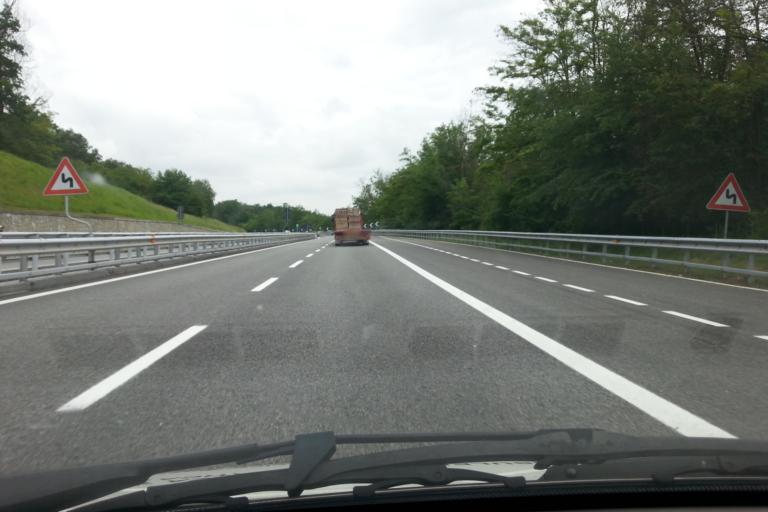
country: IT
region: Piedmont
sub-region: Provincia di Cuneo
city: Niella Tanaro
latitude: 44.4122
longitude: 7.9096
